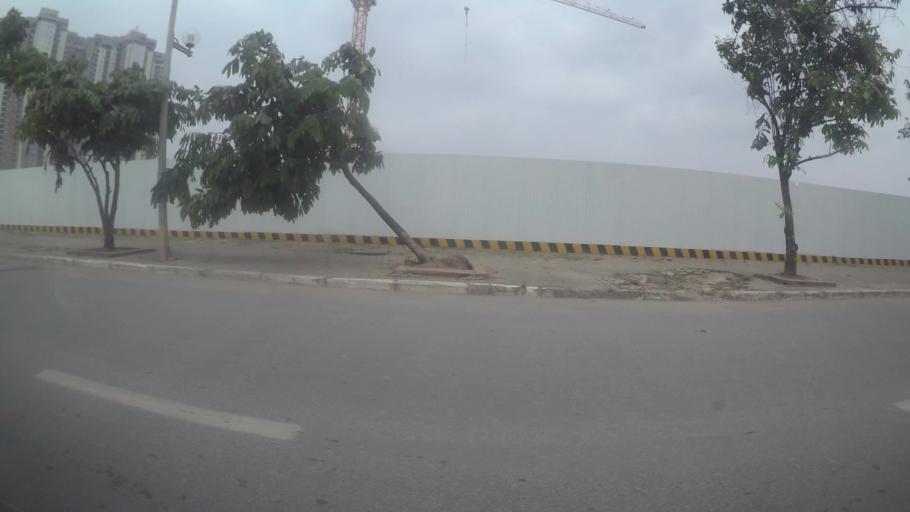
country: VN
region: Ha Noi
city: Thanh Xuan
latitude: 21.0089
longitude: 105.7740
